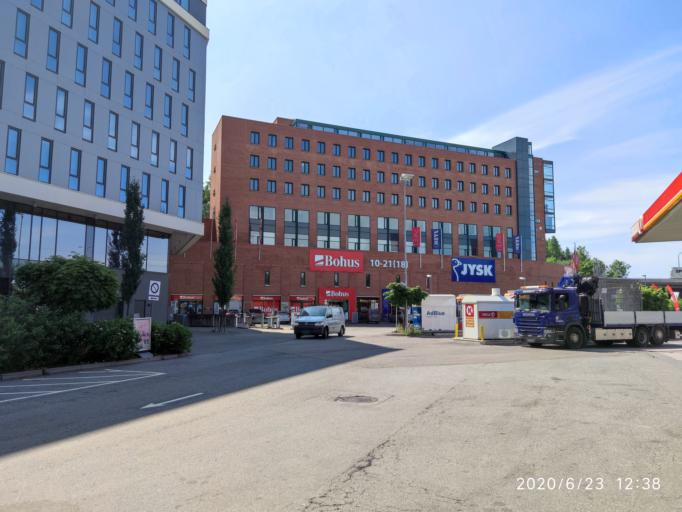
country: NO
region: Akershus
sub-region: Lorenskog
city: Kjenn
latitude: 59.9302
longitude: 10.8678
